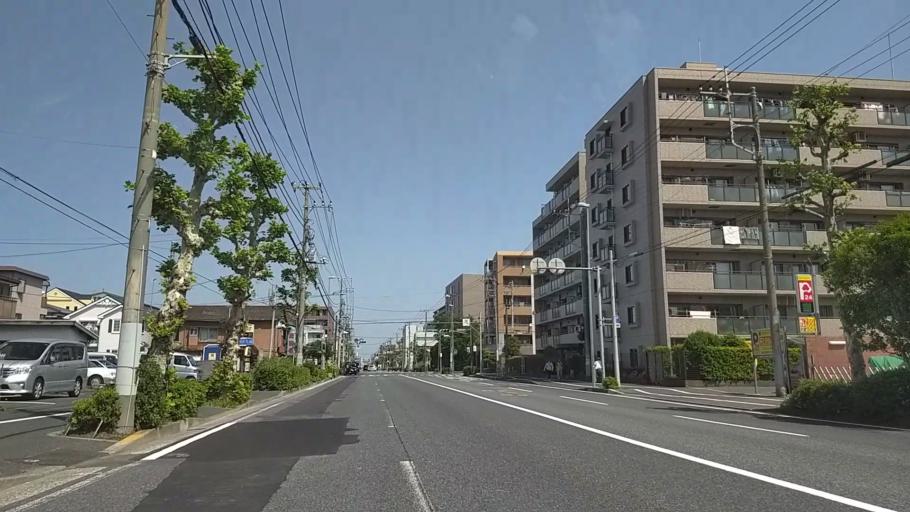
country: JP
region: Kanagawa
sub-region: Kawasaki-shi
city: Kawasaki
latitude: 35.5041
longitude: 139.6937
